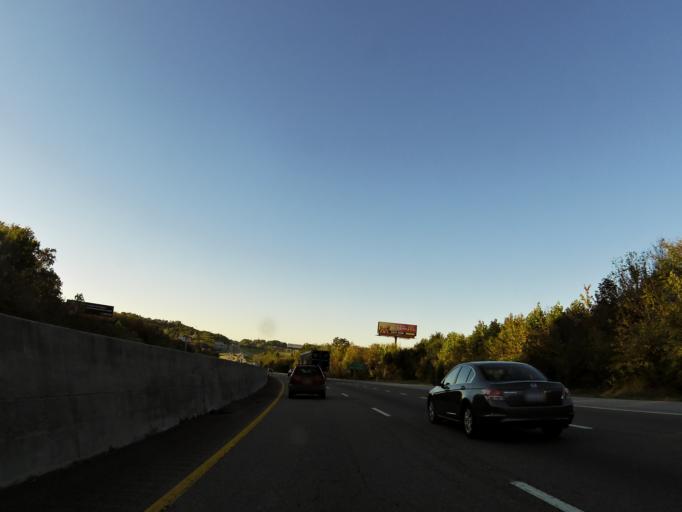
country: US
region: Tennessee
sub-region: Knox County
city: Knoxville
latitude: 36.0401
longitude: -83.9963
